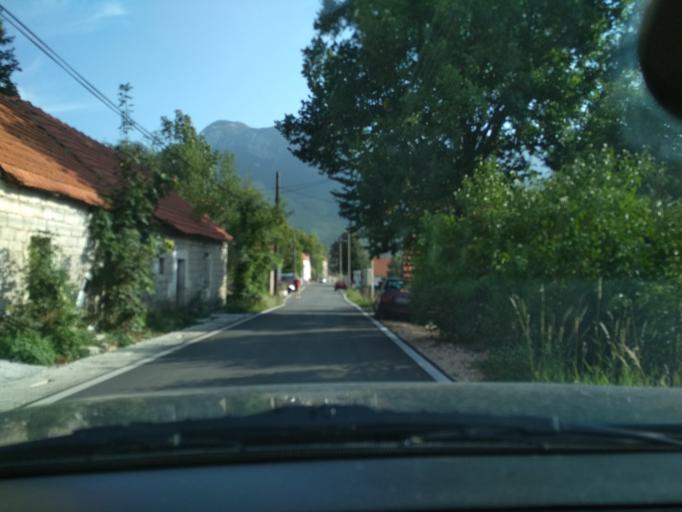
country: ME
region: Kotor
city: Kotor
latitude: 42.4352
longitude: 18.8296
